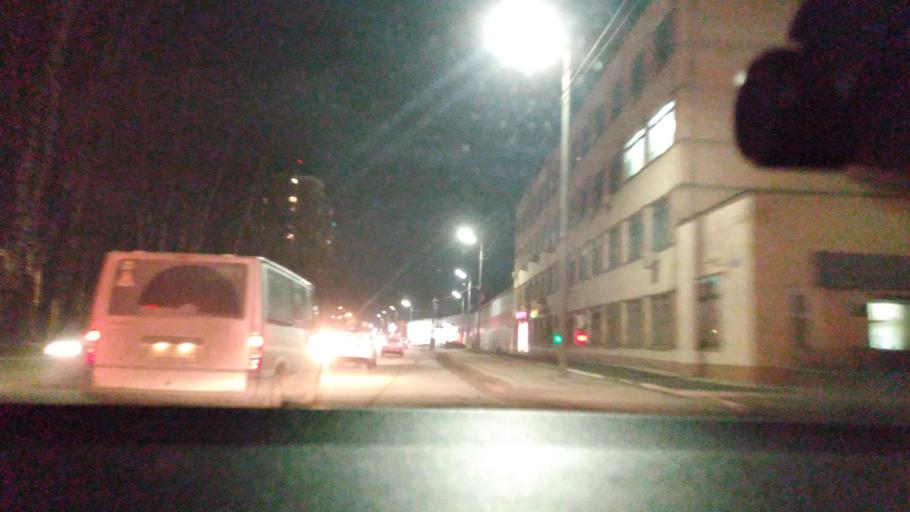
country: RU
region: Moskovskaya
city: Balashikha
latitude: 55.8195
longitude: 37.9530
